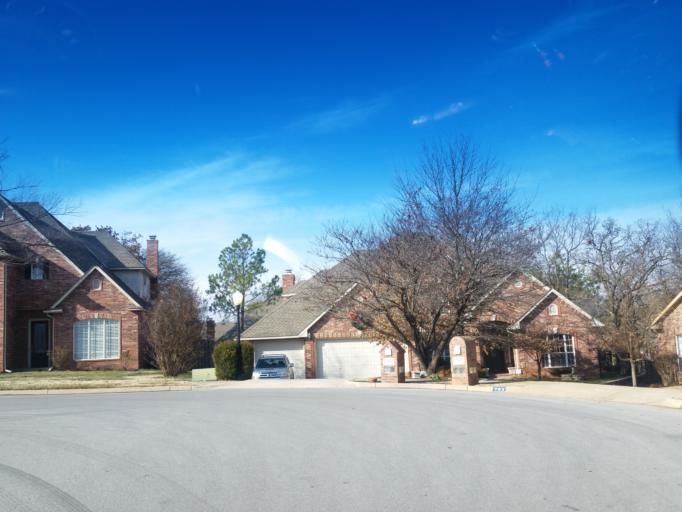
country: US
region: Oklahoma
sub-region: Oklahoma County
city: Edmond
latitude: 35.6472
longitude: -97.4297
